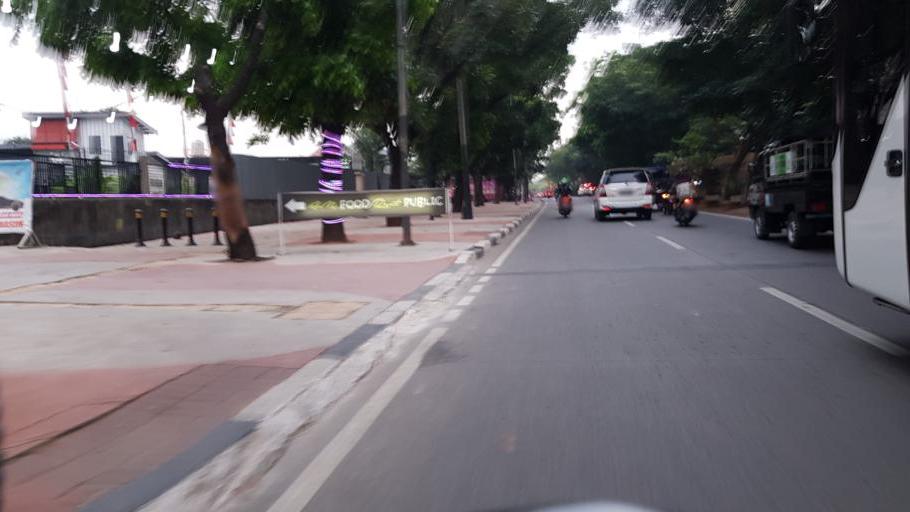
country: ID
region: Jakarta Raya
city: Jakarta
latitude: -6.3067
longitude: 106.8916
